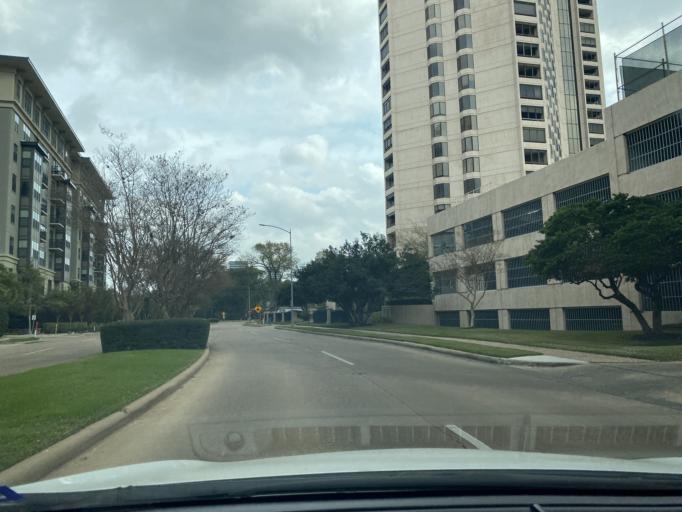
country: US
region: Texas
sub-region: Harris County
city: Hunters Creek Village
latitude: 29.7459
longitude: -95.4724
